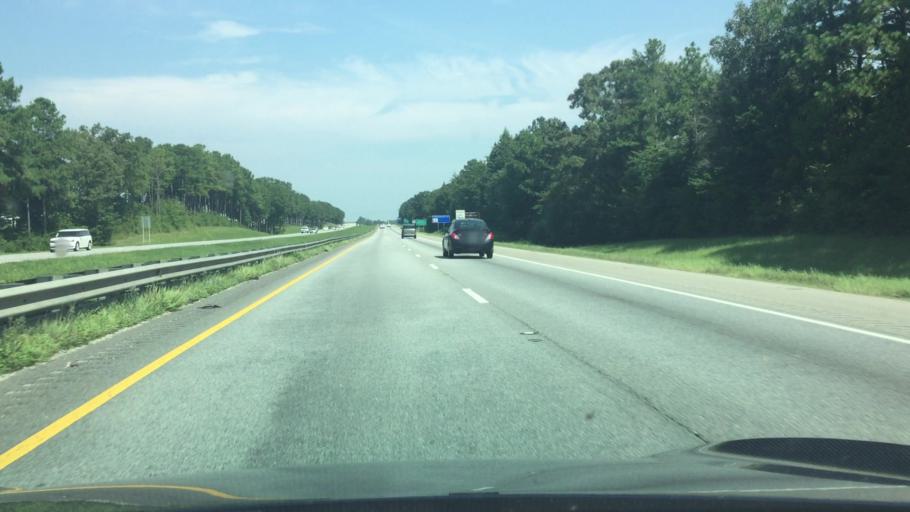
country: US
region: Alabama
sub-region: Shelby County
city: Calera
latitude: 33.1587
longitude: -86.7702
